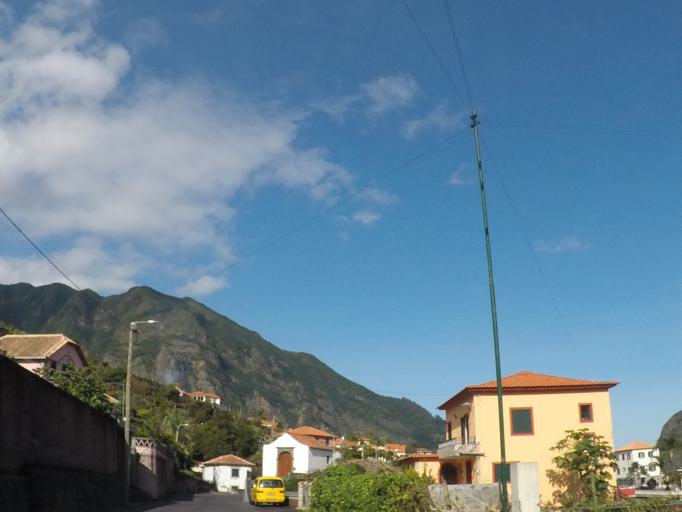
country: PT
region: Madeira
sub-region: Sao Vicente
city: Sao Vicente
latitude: 32.7870
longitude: -17.0343
